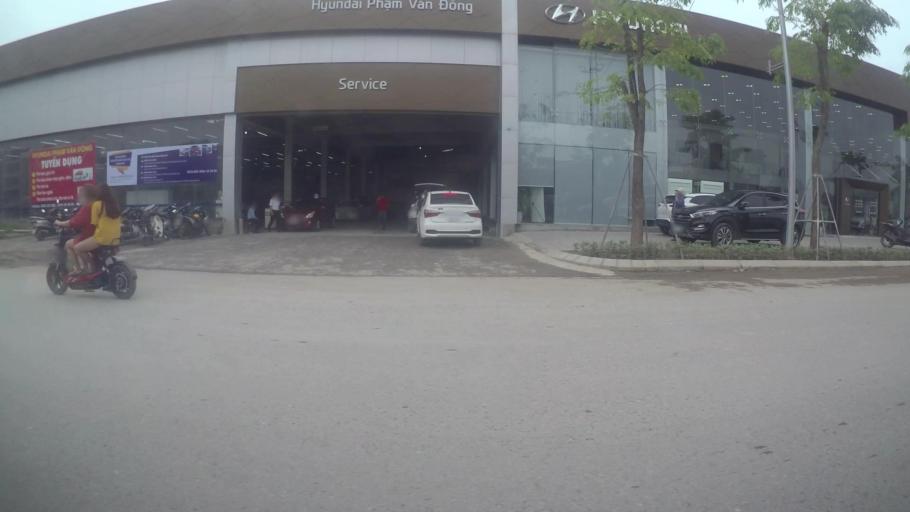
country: VN
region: Ha Noi
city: Tay Ho
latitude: 21.0745
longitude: 105.7856
